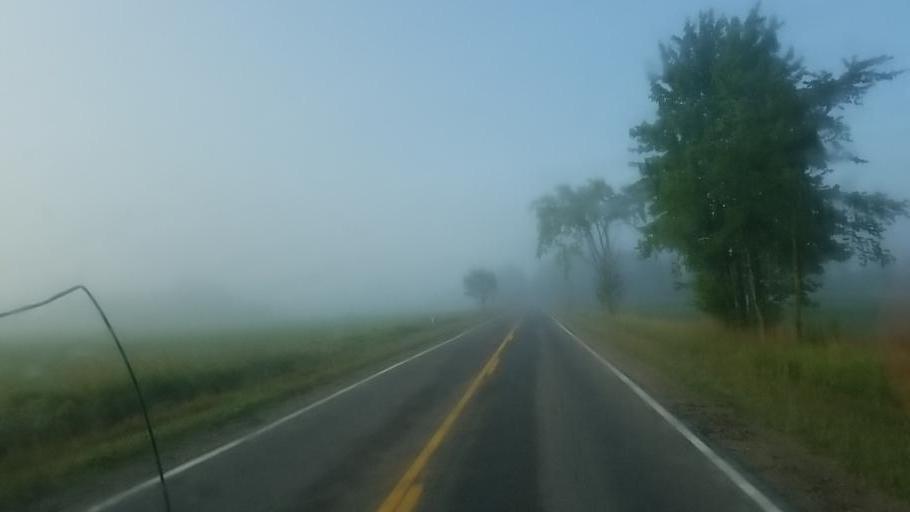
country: US
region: Michigan
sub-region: Muskegon County
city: Twin Lake
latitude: 43.4632
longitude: -86.0791
